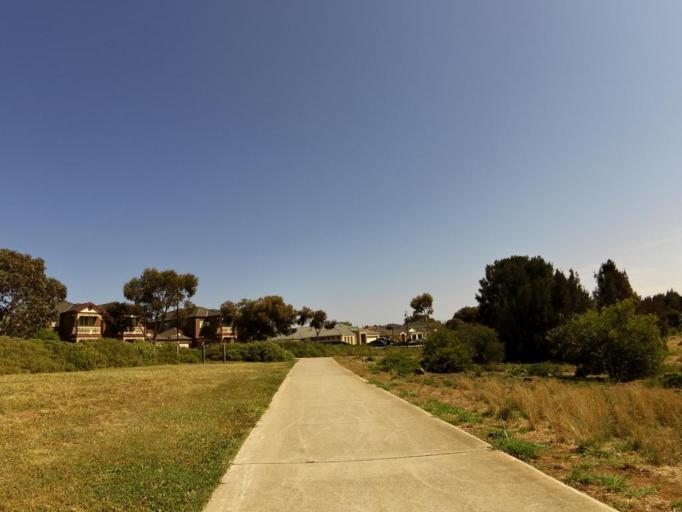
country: AU
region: Victoria
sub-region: Wyndham
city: Williams Landing
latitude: -37.8756
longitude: 144.7418
